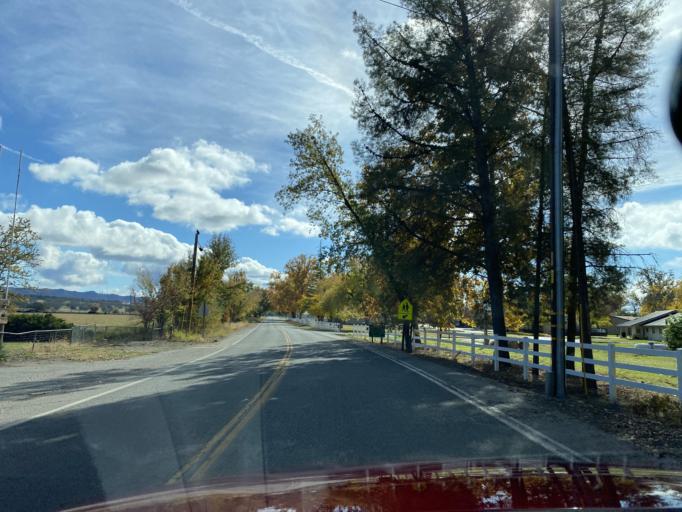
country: US
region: California
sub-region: Colusa County
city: Maxwell
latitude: 39.3799
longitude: -122.5505
